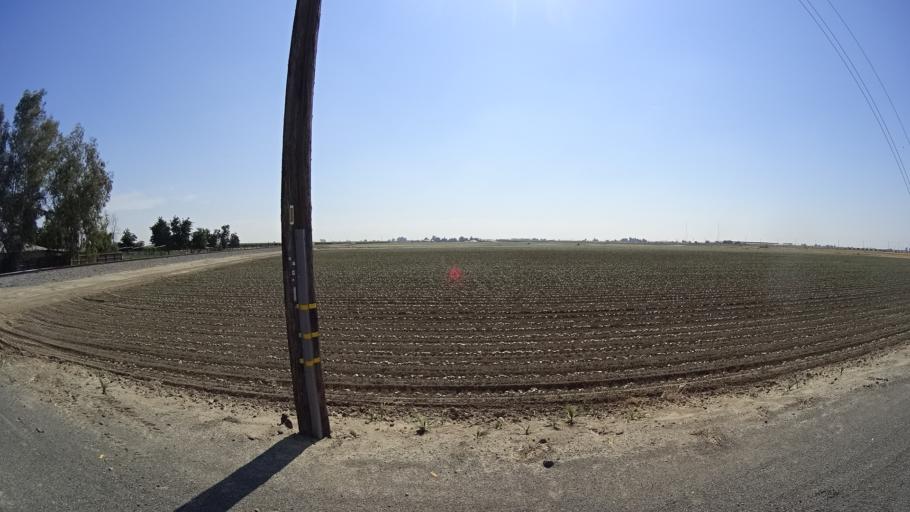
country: US
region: California
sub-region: Kings County
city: Home Garden
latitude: 36.3344
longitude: -119.5830
